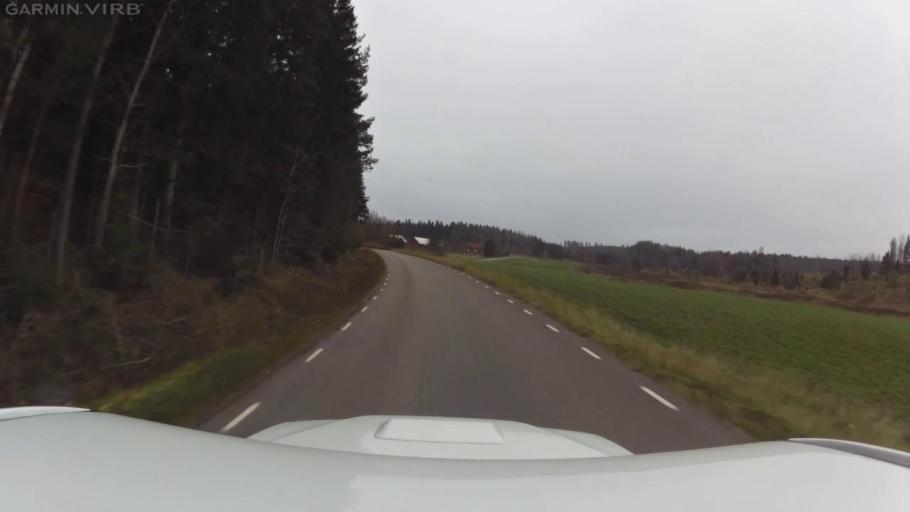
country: SE
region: OEstergoetland
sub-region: Linkopings Kommun
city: Vikingstad
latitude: 58.2209
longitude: 15.3981
